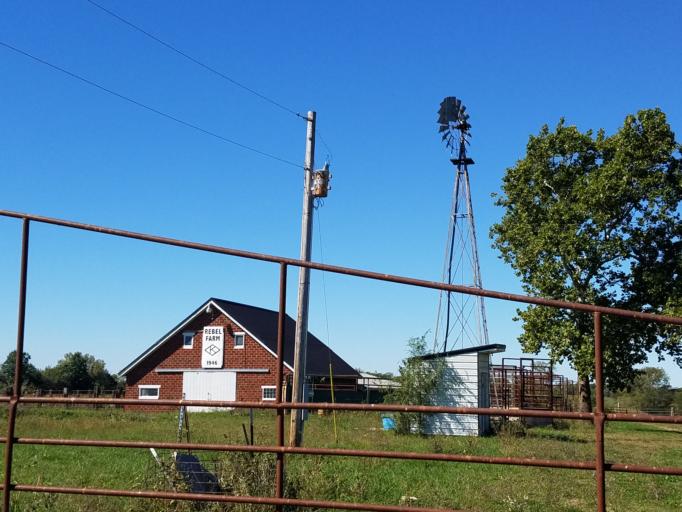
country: US
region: Missouri
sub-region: Mercer County
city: Princeton
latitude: 40.3945
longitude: -93.6800
